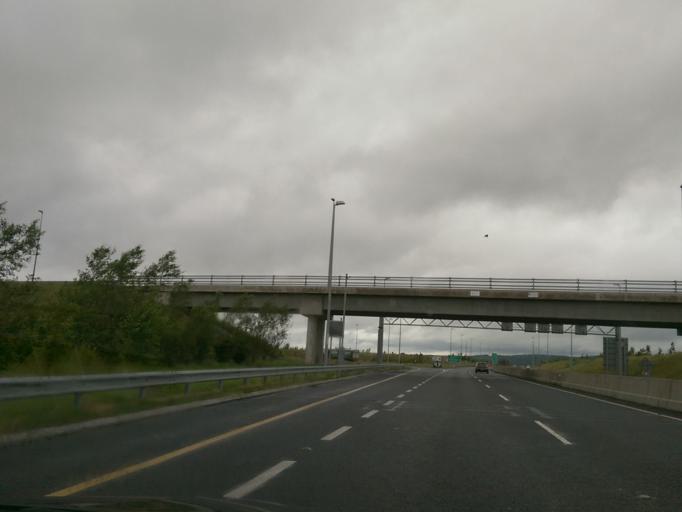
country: IE
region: Munster
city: Moyross
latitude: 52.6600
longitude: -8.6930
